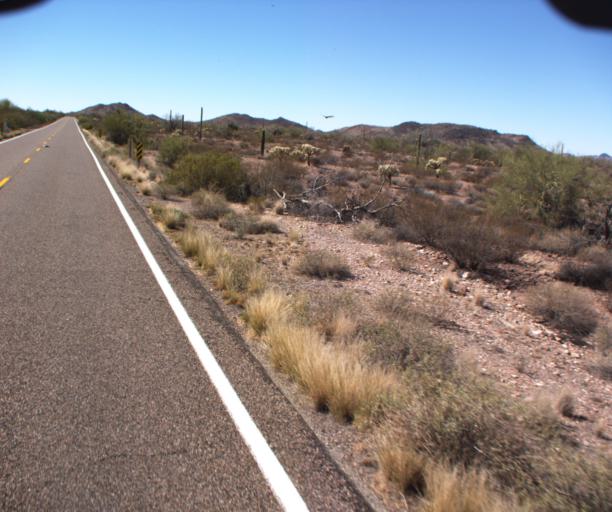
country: MX
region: Sonora
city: Sonoyta
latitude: 32.1084
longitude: -112.7702
